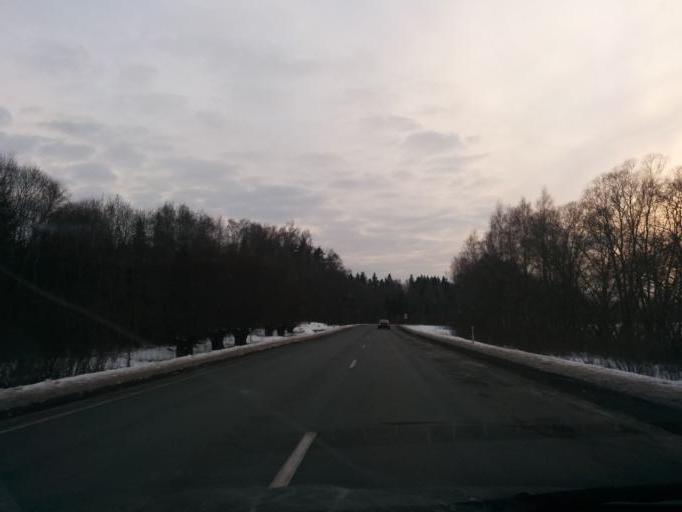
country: LV
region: Amatas Novads
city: Drabesi
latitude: 57.2472
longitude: 25.3317
